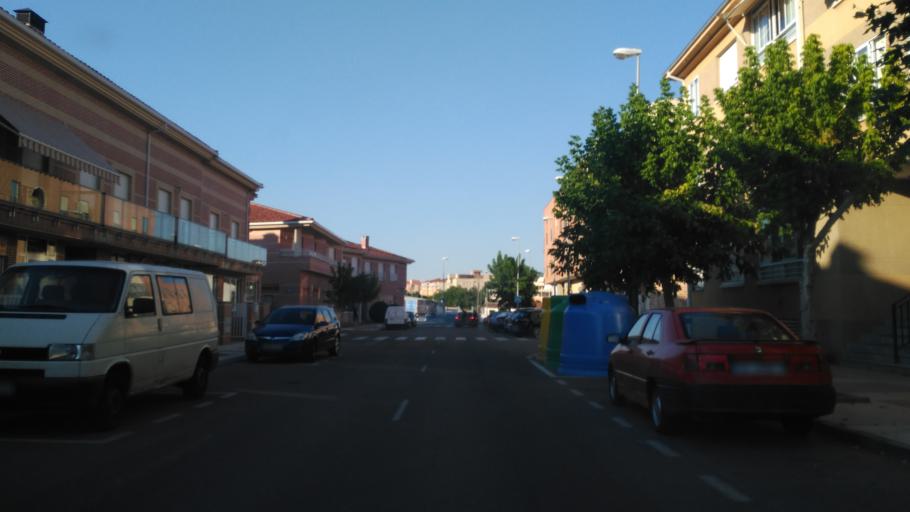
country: ES
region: Castille and Leon
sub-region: Provincia de Salamanca
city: Carbajosa de la Sagrada
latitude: 40.9334
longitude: -5.6523
